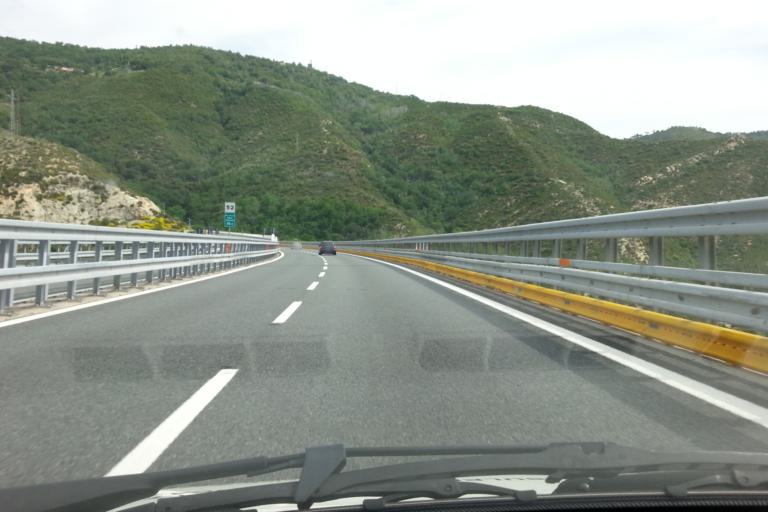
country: IT
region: Liguria
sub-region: Provincia di Savona
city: Spotorno
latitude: 44.2320
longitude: 8.3995
